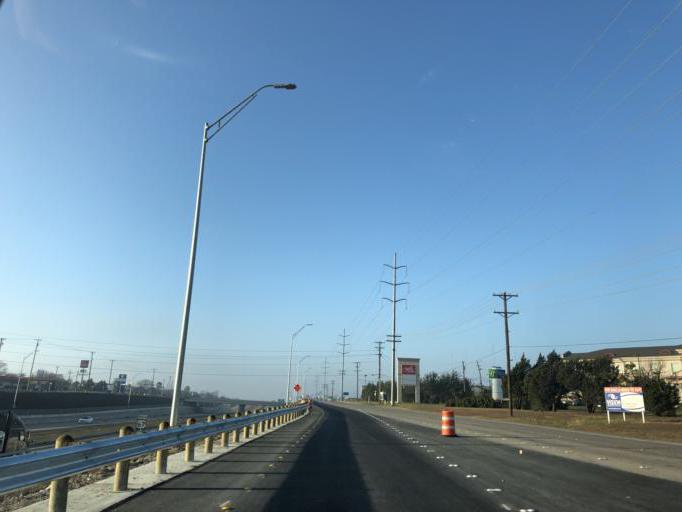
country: US
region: Texas
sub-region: Dallas County
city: Cedar Hill
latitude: 32.6072
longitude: -96.9292
